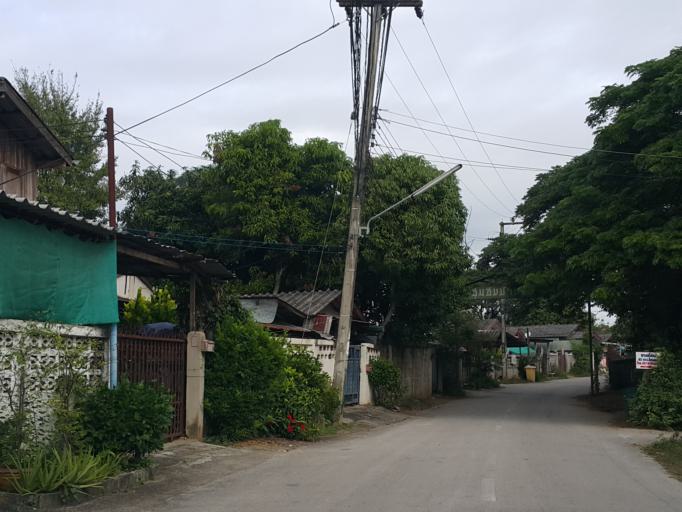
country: TH
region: Lampang
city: Lampang
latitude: 18.3025
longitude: 99.5033
